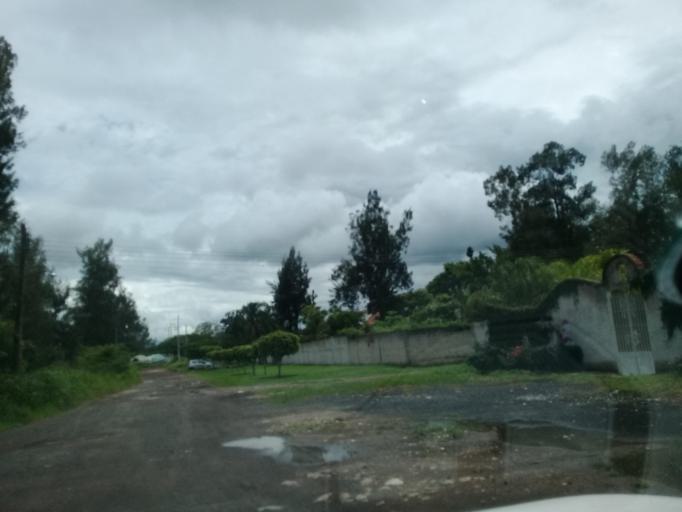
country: MX
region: Veracruz
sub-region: Emiliano Zapata
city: Dos Rios
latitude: 19.4812
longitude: -96.7929
